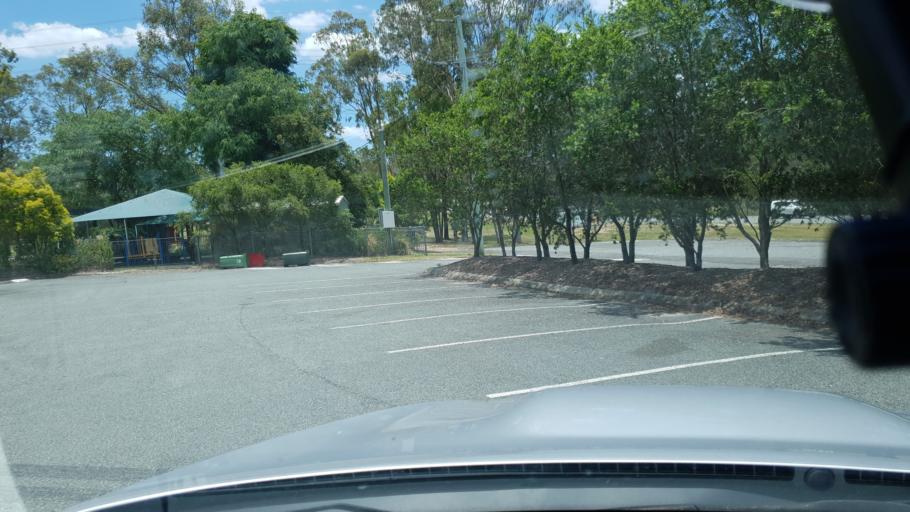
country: AU
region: Queensland
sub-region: Logan
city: Park Ridge South
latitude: -27.7303
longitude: 152.9837
